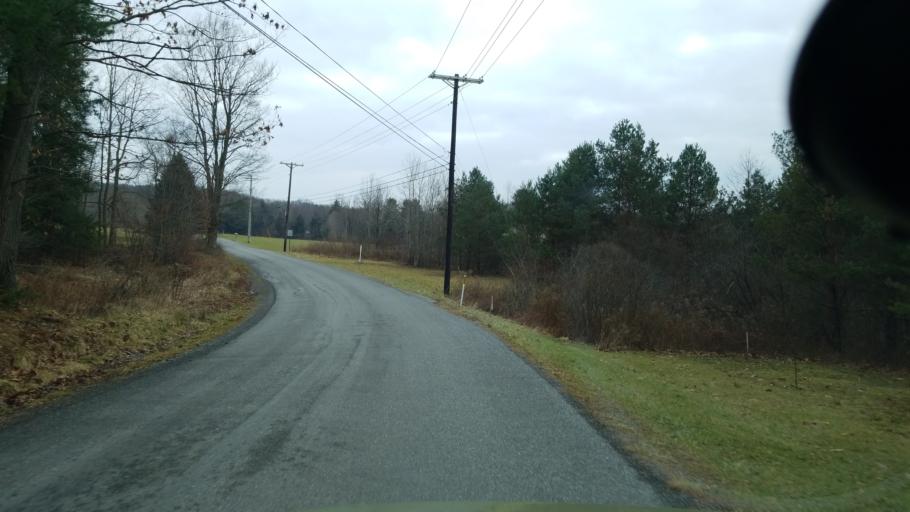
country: US
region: Pennsylvania
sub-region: Clearfield County
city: Treasure Lake
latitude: 41.1190
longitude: -78.6913
